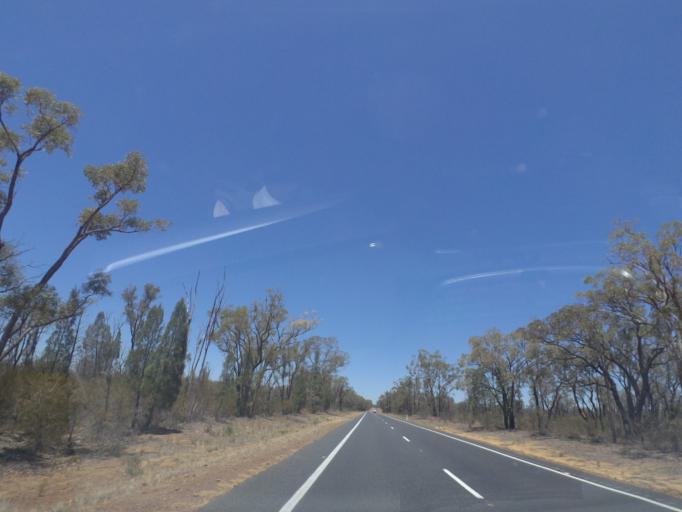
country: AU
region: New South Wales
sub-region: Narrabri
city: Narrabri
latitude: -30.7458
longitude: 149.5131
